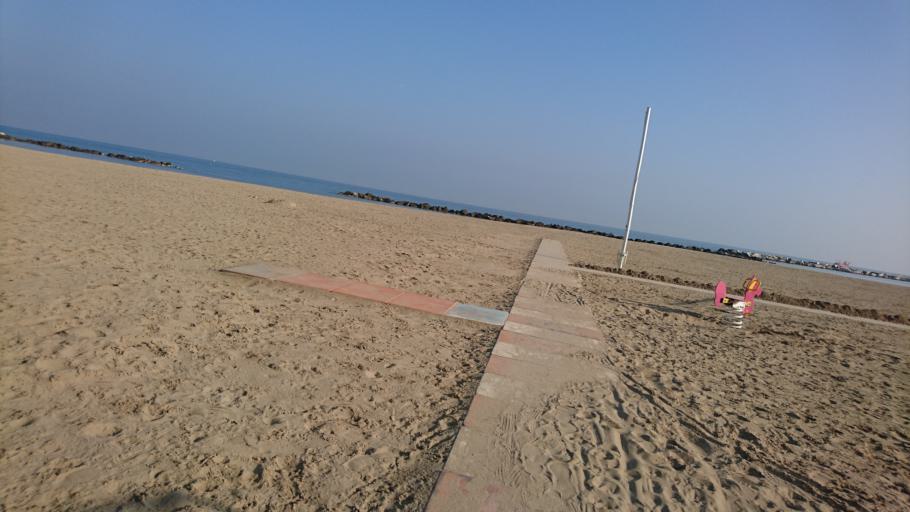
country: IT
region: Emilia-Romagna
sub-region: Provincia di Rimini
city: Rimini
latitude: 44.0768
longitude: 12.5585
